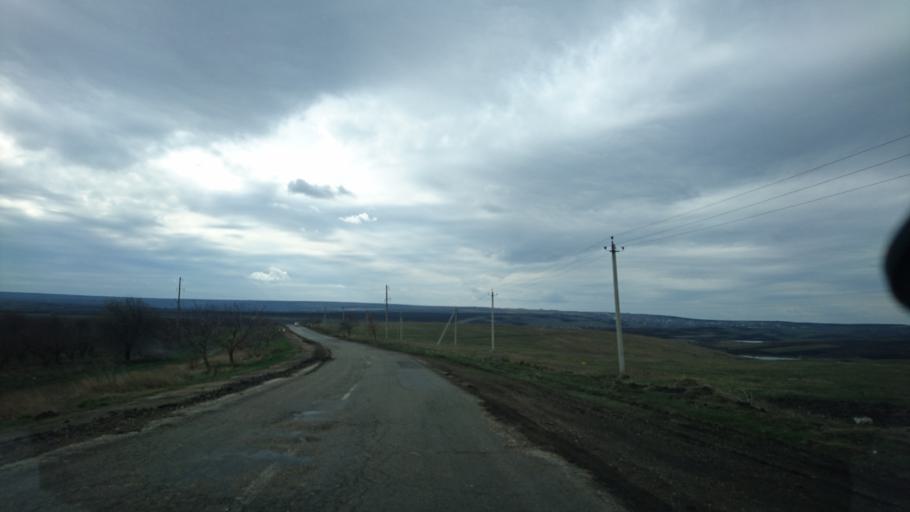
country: MD
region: Cantemir
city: Visniovca
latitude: 46.3291
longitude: 28.4680
